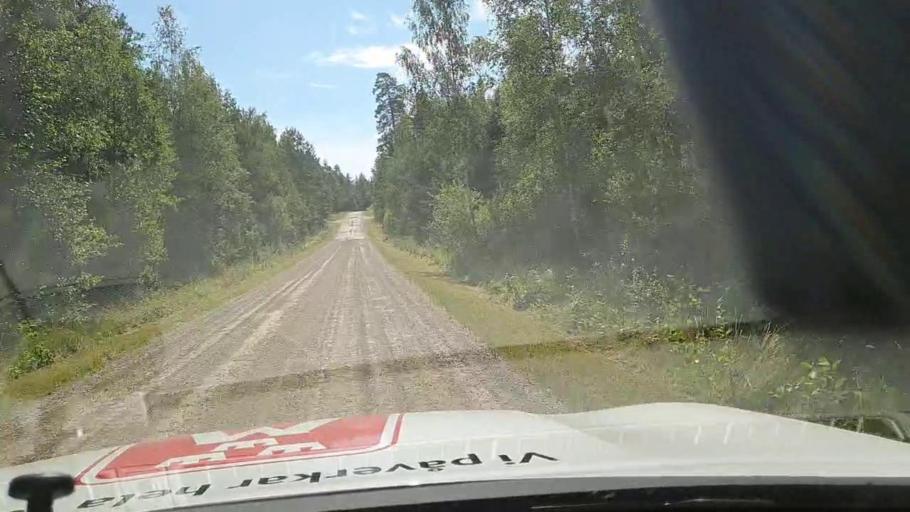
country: SE
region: Soedermanland
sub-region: Strangnas Kommun
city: Akers Styckebruk
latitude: 59.2188
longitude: 16.9083
